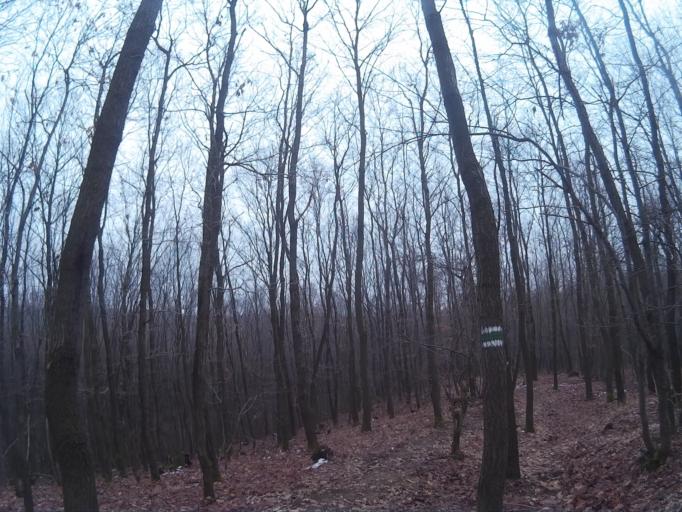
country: HU
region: Komarom-Esztergom
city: Tardos
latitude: 47.6541
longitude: 18.4909
